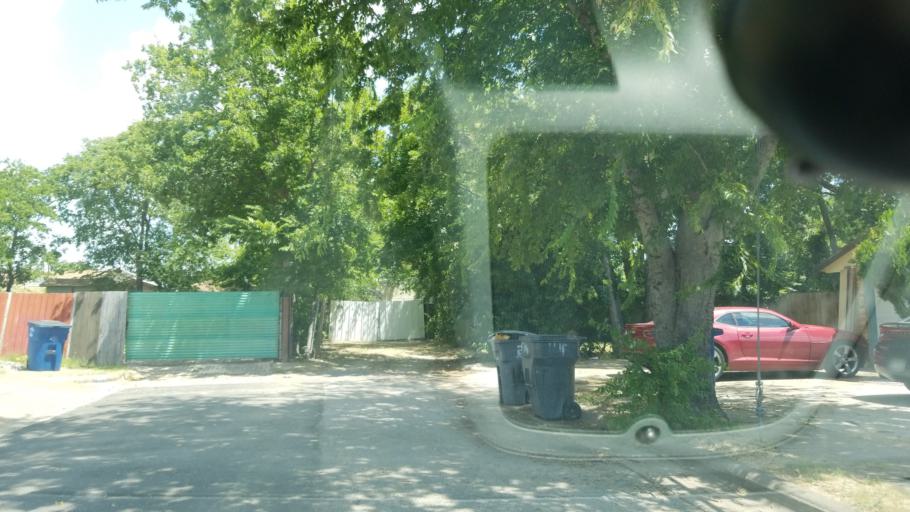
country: US
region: Texas
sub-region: Dallas County
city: Cockrell Hill
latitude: 32.7296
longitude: -96.8390
